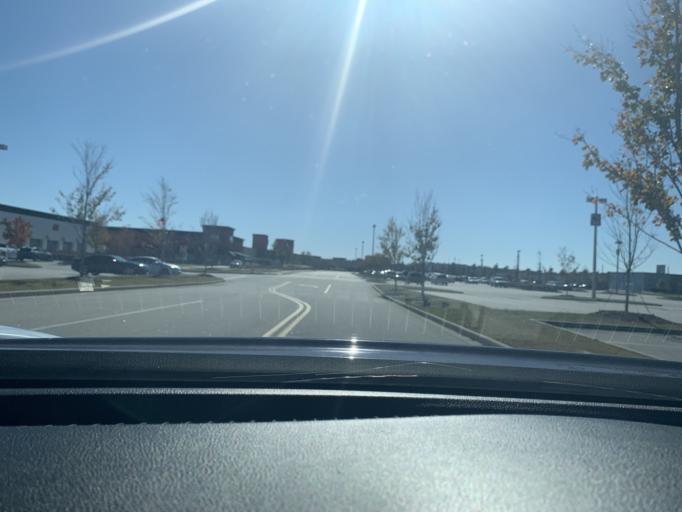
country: US
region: Georgia
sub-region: Chatham County
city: Pooler
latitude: 32.1371
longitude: -81.2445
